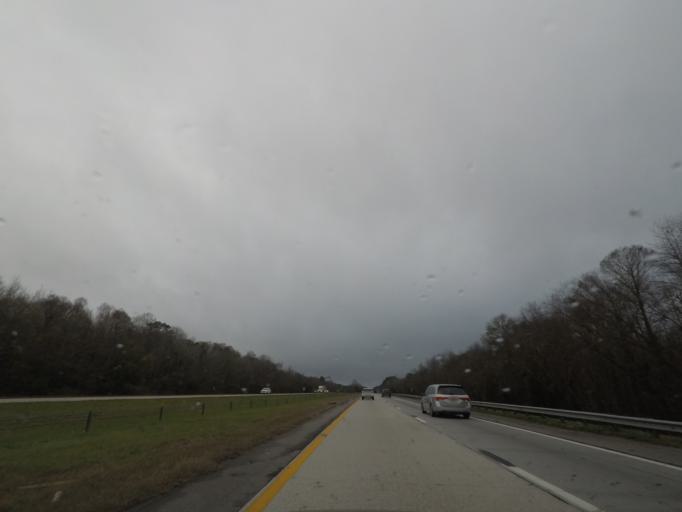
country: US
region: South Carolina
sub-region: Dorchester County
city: Saint George
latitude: 33.0939
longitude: -80.6482
